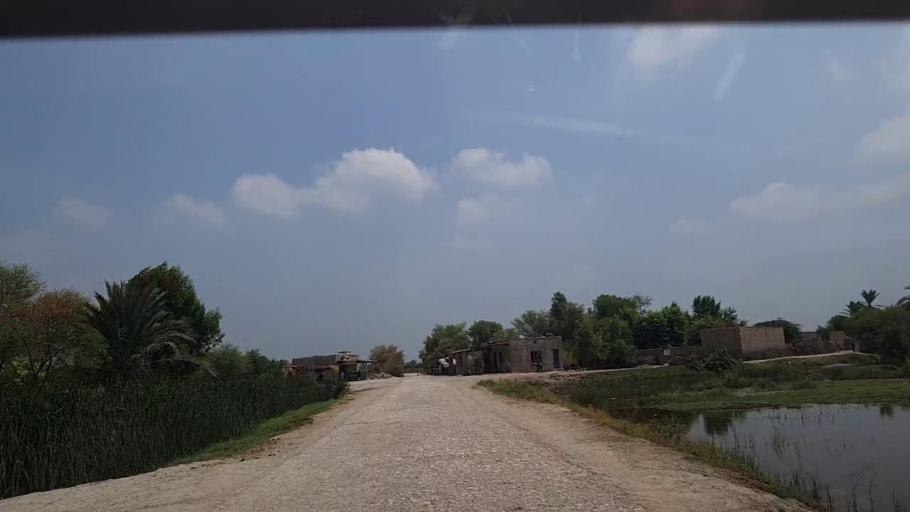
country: PK
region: Sindh
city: Khanpur
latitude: 27.8981
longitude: 69.3948
